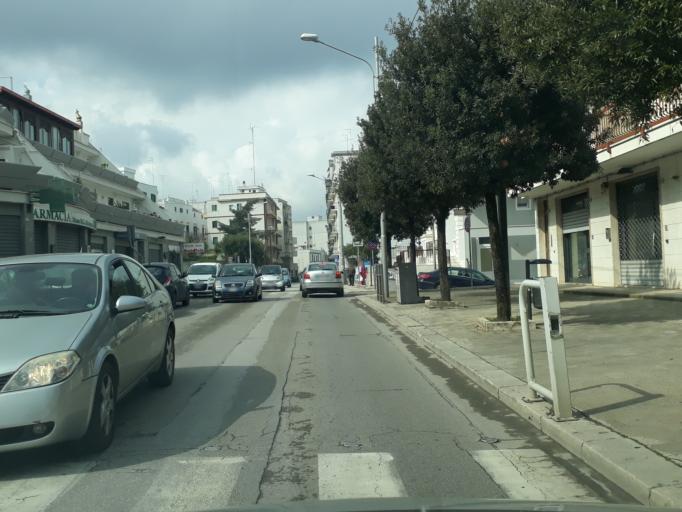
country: IT
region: Apulia
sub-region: Provincia di Bari
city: Locorotondo
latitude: 40.7545
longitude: 17.3305
